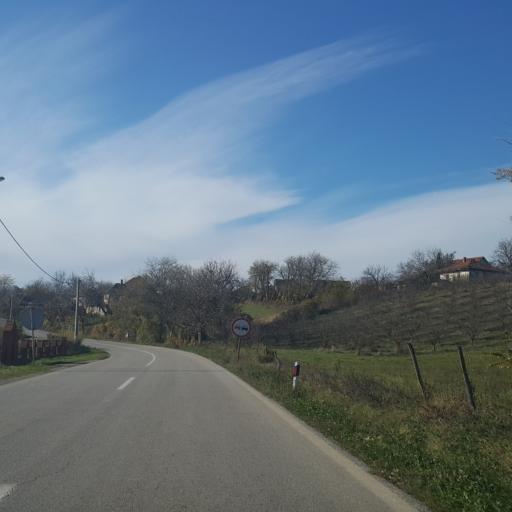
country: RS
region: Central Serbia
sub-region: Sumadijski Okrug
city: Topola
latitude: 44.2490
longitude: 20.7300
